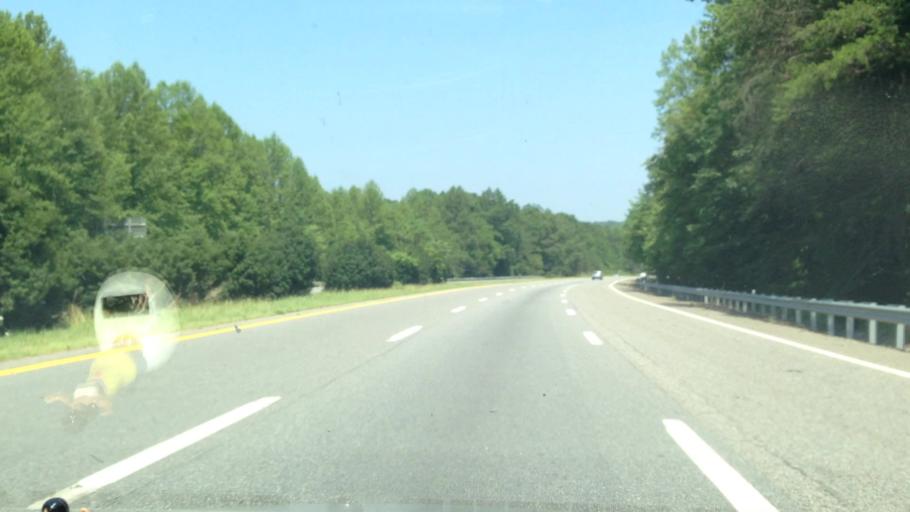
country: US
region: Virginia
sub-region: Henry County
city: Horse Pasture
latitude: 36.6503
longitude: -79.9183
